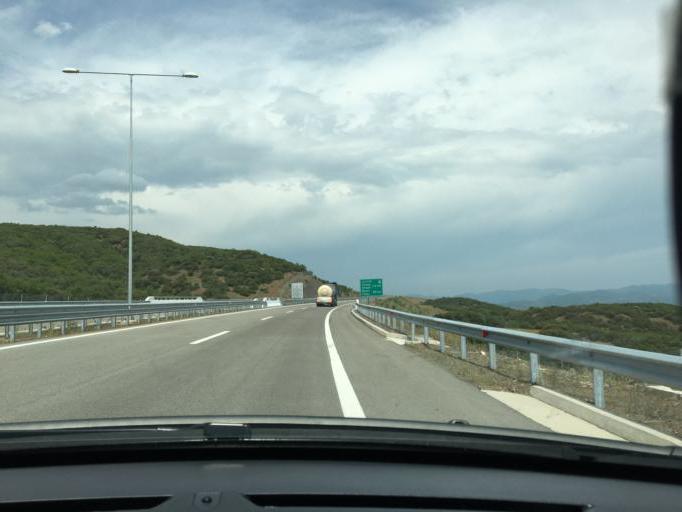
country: MK
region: Gevgelija
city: Miravci
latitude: 41.3008
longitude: 22.4285
